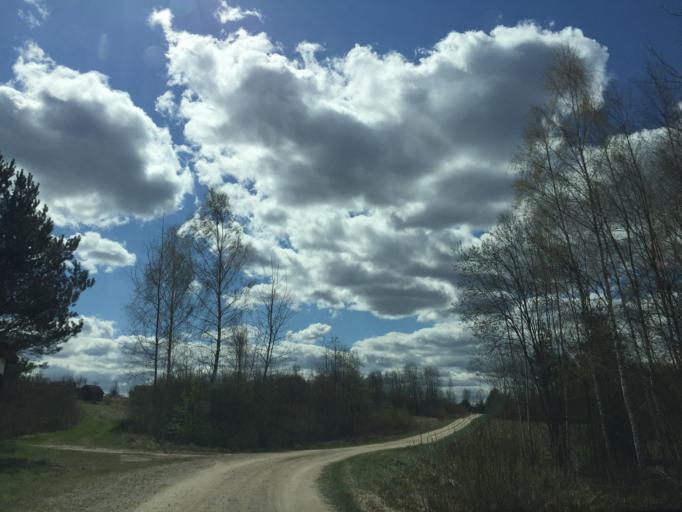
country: LV
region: Rezekne
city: Rezekne
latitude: 56.5704
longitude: 27.1454
